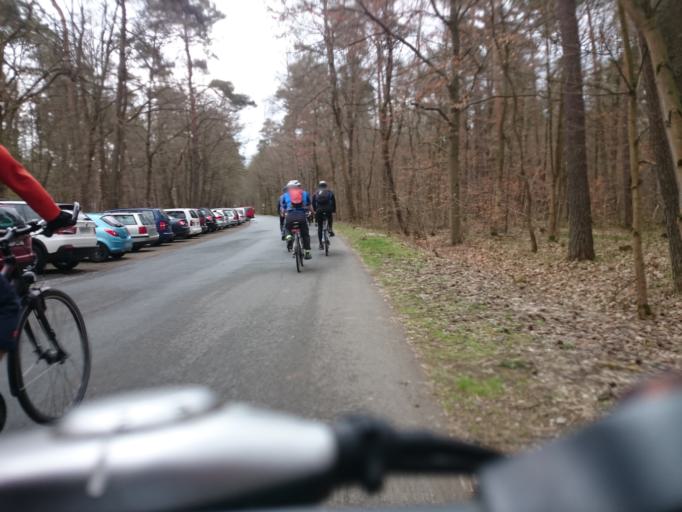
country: DE
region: Bavaria
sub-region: Regierungsbezirk Mittelfranken
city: Nuernberg
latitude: 49.4467
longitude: 11.1377
